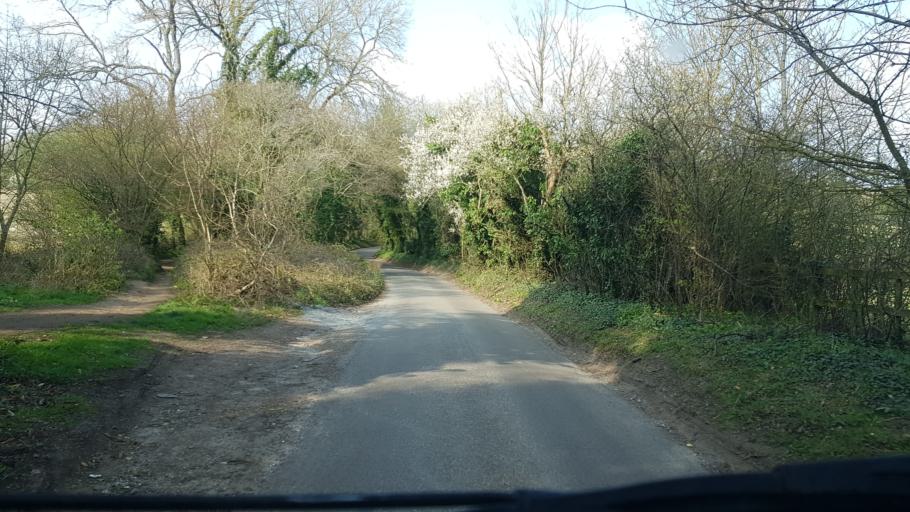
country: GB
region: England
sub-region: Surrey
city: Chilworth
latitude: 51.2287
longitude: -0.5205
